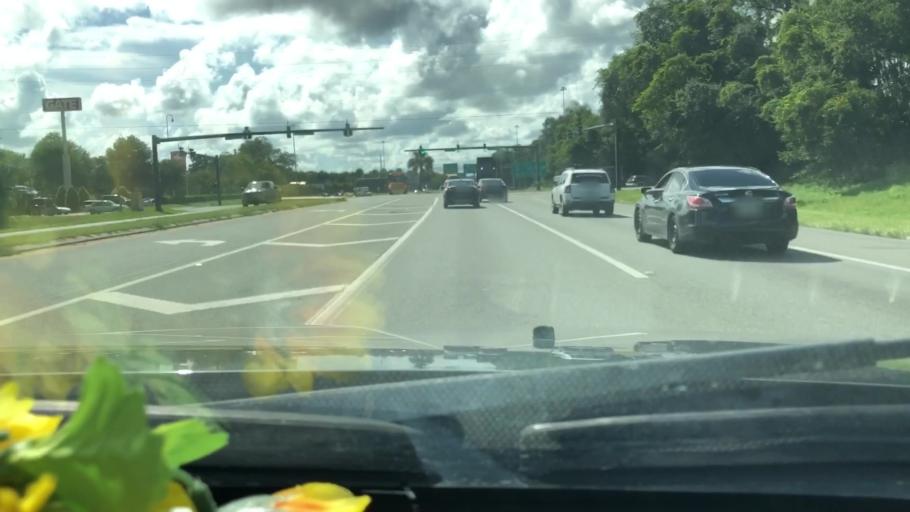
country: US
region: Florida
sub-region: Duval County
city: Jacksonville
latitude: 30.4114
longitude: -81.5592
